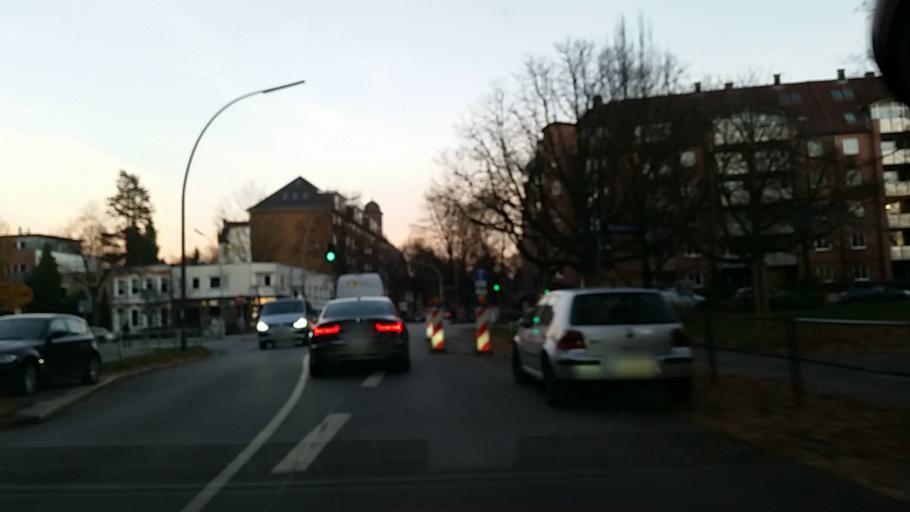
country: DE
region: Hamburg
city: Barmbek-Nord
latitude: 53.5916
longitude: 10.0490
